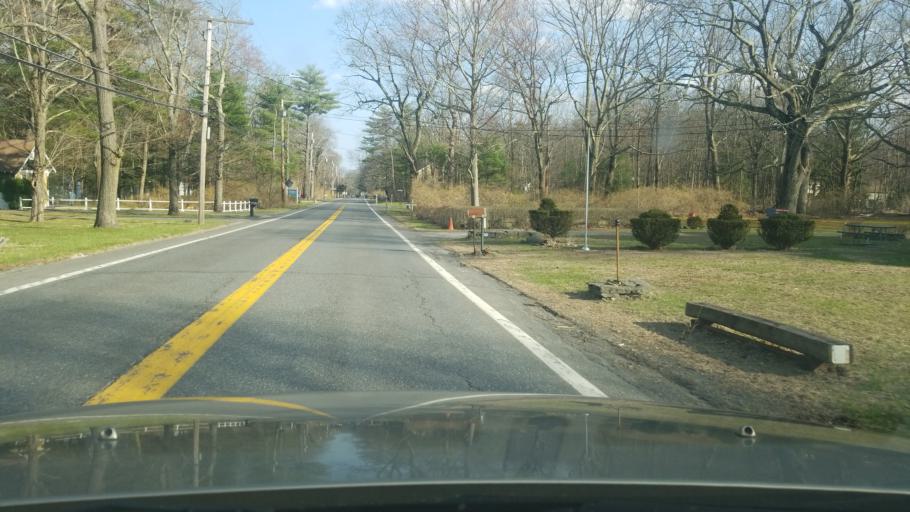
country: US
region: New York
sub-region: Greene County
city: Palenville
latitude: 42.1656
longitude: -74.0142
